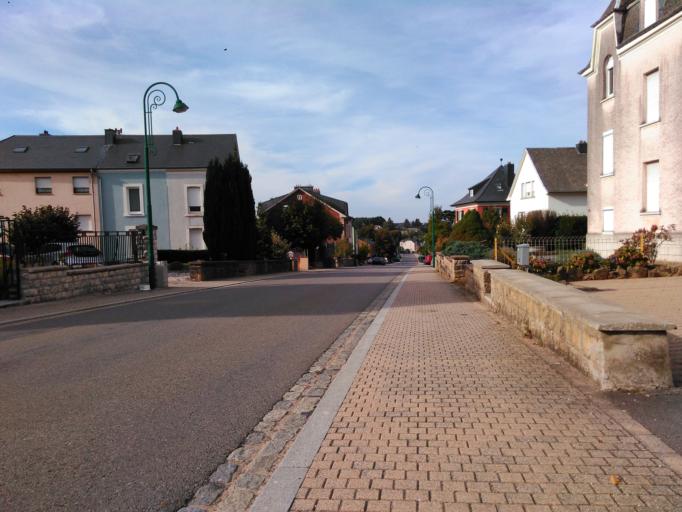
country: LU
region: Luxembourg
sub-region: Canton de Capellen
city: Steinfort
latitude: 49.6398
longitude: 5.9160
